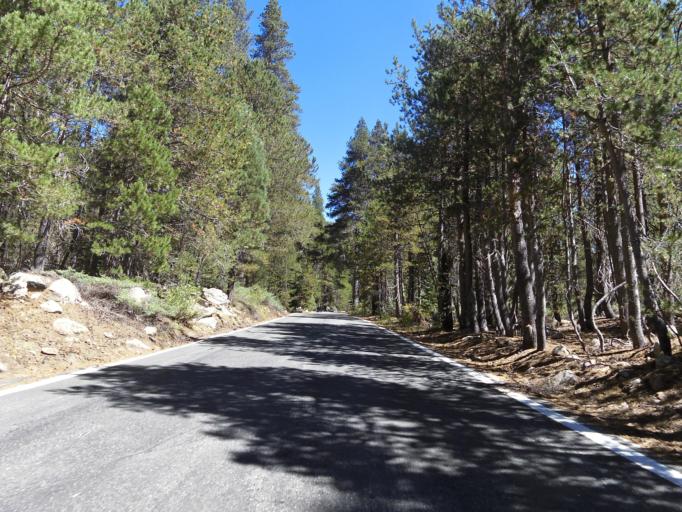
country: US
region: Nevada
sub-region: Douglas County
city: Gardnerville Ranchos
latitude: 38.5402
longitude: -119.8902
